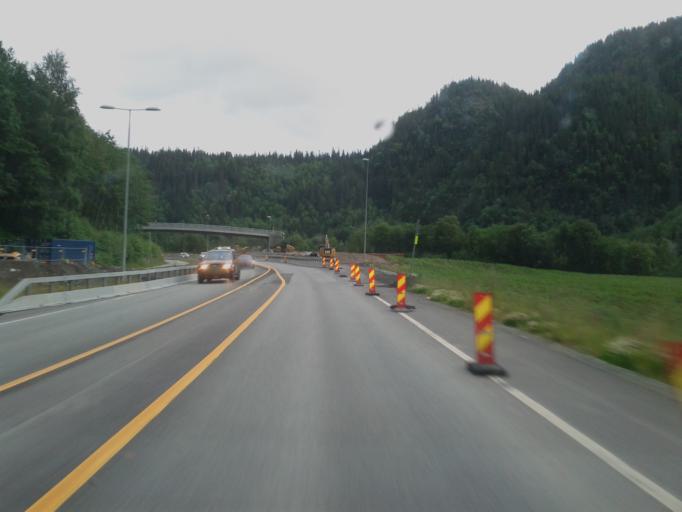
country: NO
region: Sor-Trondelag
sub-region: Midtre Gauldal
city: Storen
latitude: 63.0719
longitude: 10.2665
